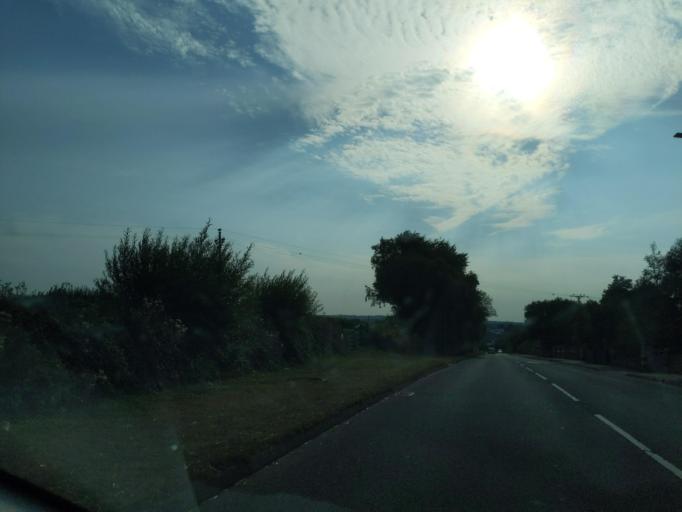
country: GB
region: England
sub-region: Devon
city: Great Torrington
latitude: 50.9551
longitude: -4.1250
